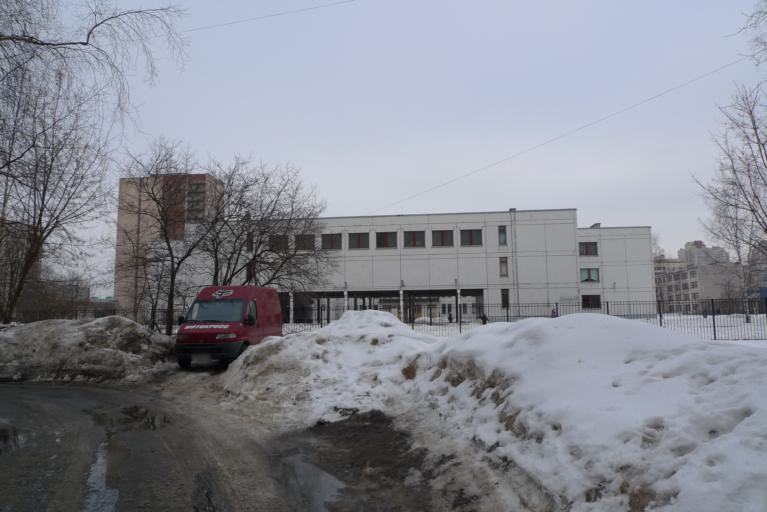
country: RU
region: St.-Petersburg
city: Ozerki
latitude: 60.0461
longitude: 30.3347
